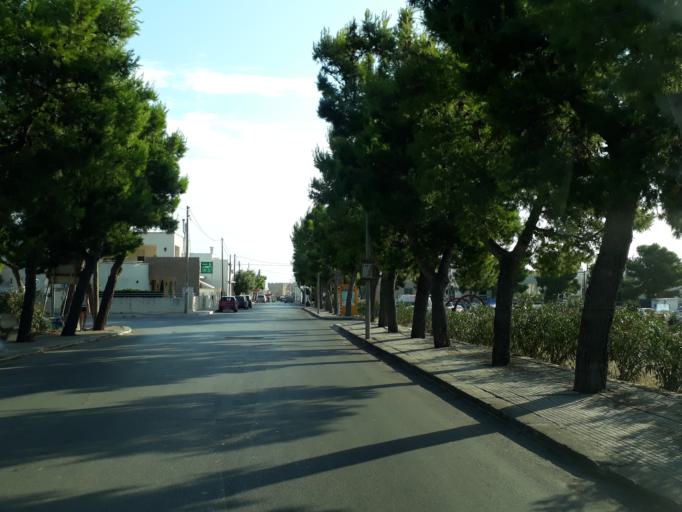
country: IT
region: Apulia
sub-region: Provincia di Brindisi
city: Carovigno
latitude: 40.7552
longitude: 17.7003
